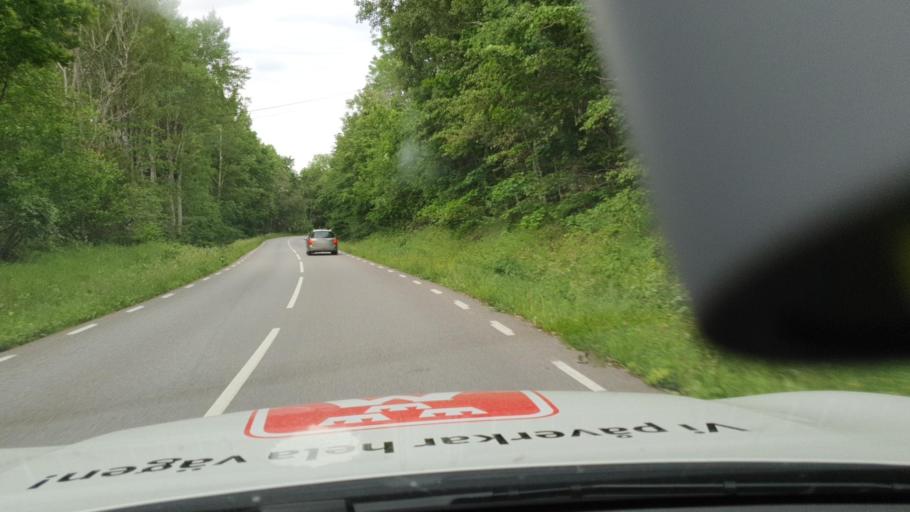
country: SE
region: Vaestra Goetaland
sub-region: Karlsborgs Kommun
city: Karlsborg
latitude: 58.7519
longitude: 14.5091
